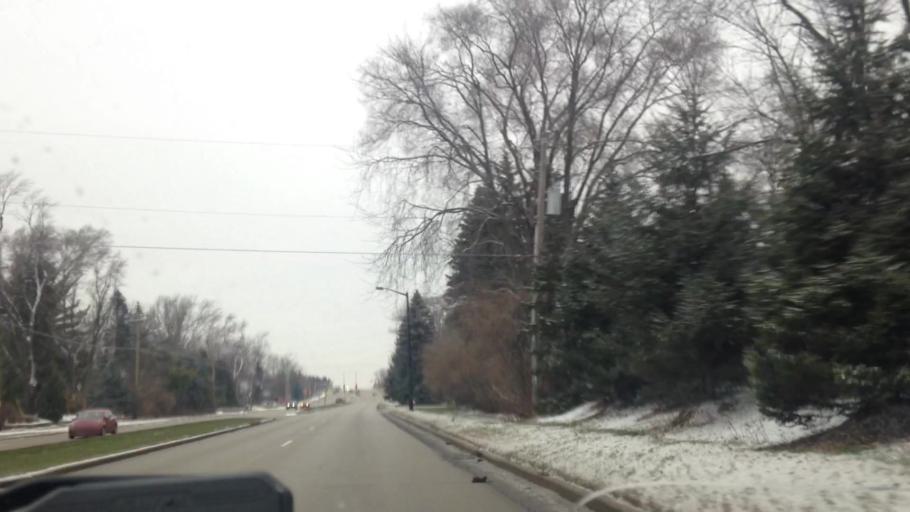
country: US
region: Wisconsin
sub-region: Waukesha County
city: Butler
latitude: 43.1208
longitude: -88.1051
